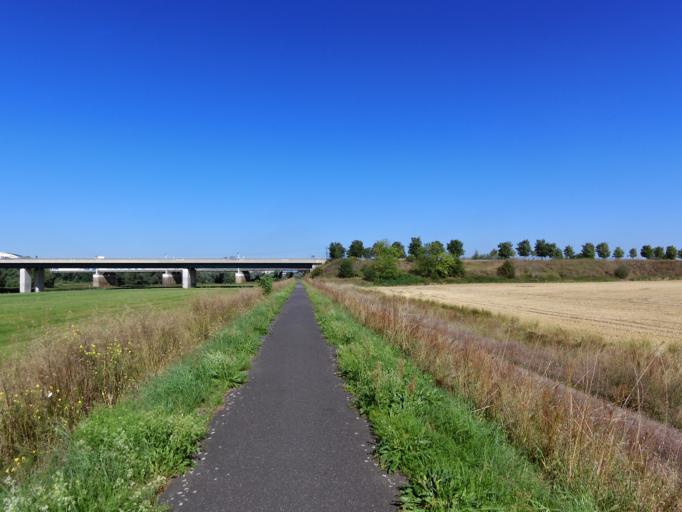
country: DE
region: Saxony
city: Riesa
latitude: 51.3109
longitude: 13.3001
